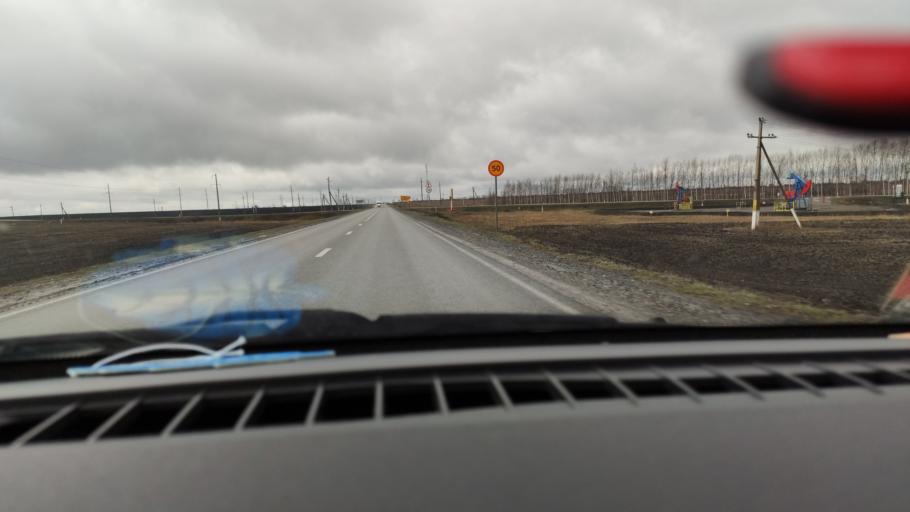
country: RU
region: Tatarstan
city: Nurlat
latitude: 54.4568
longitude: 50.8291
